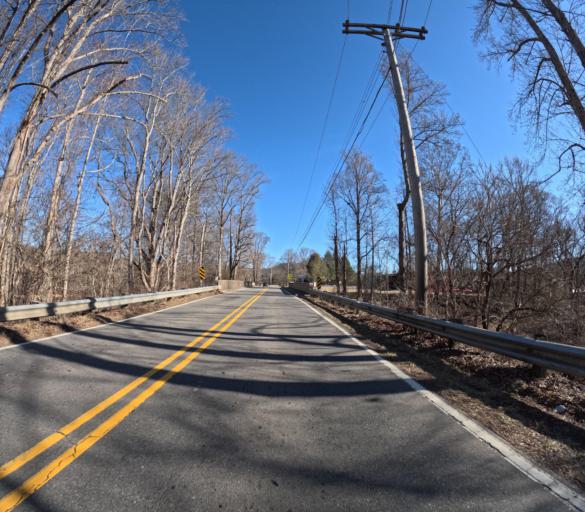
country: US
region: North Carolina
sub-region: Cherokee County
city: Murphy
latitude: 35.0914
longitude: -84.0385
